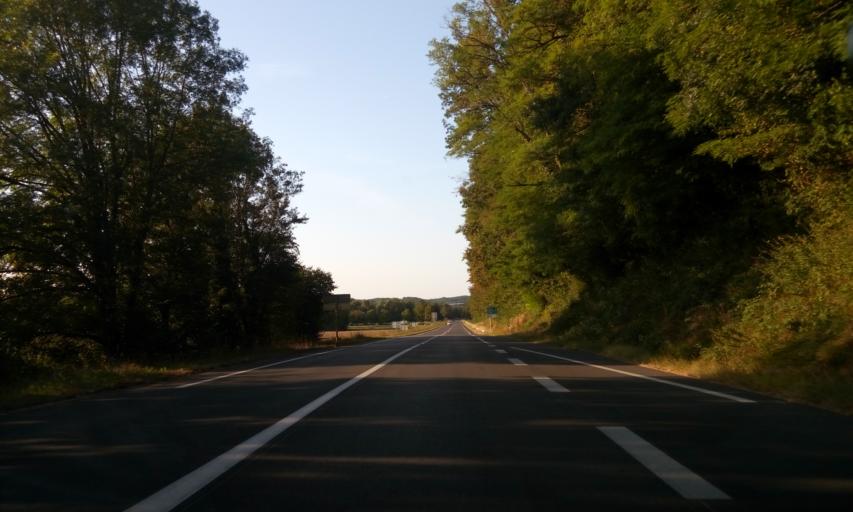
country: FR
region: Rhone-Alpes
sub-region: Departement de l'Ain
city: Neuville-sur-Ain
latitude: 46.0600
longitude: 5.3863
